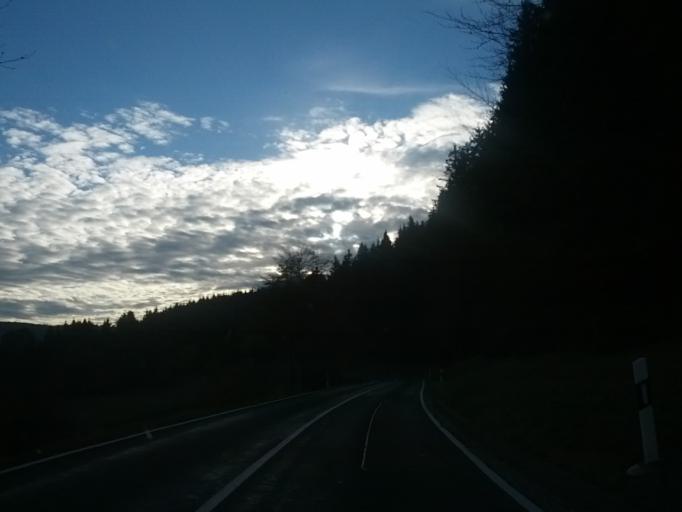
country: DE
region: Thuringia
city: Brotterode
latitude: 50.8346
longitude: 10.4646
